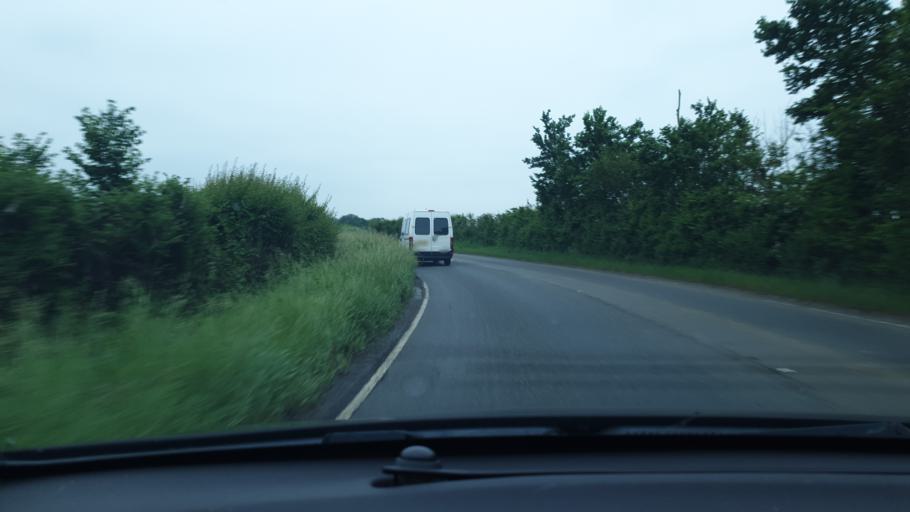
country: GB
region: England
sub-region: Essex
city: Little Clacton
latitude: 51.8706
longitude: 1.1733
